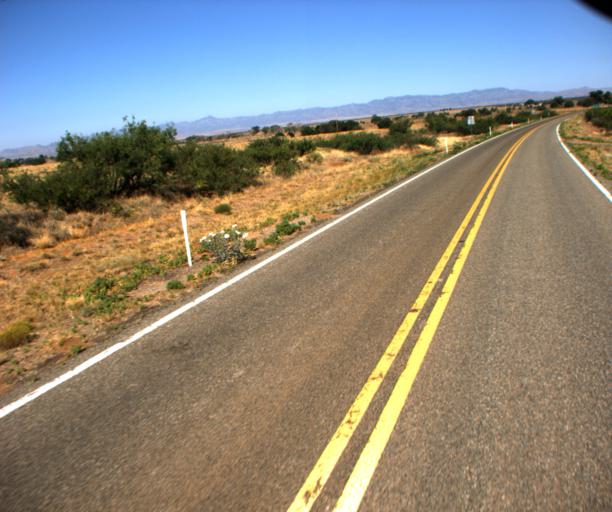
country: US
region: Arizona
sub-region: Graham County
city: Swift Trail Junction
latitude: 32.5826
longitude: -109.9555
